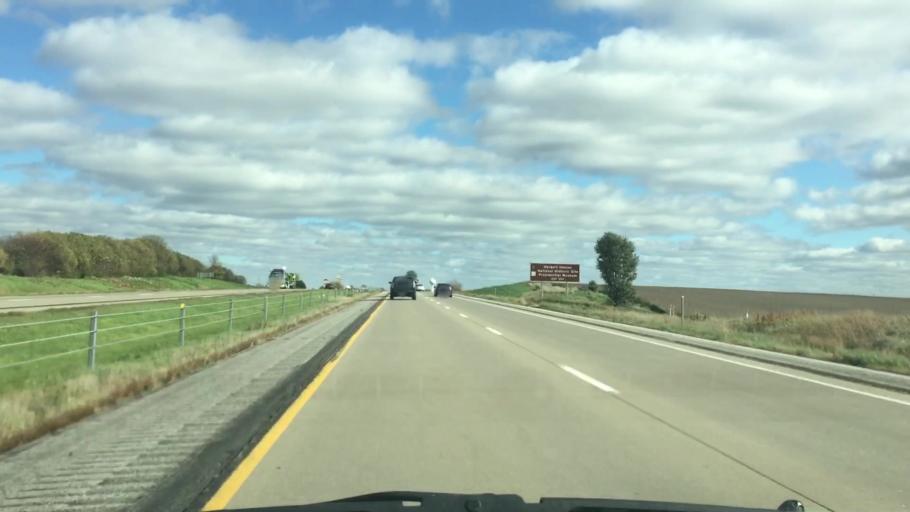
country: US
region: Iowa
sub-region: Cedar County
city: West Branch
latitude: 41.6654
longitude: -91.3637
